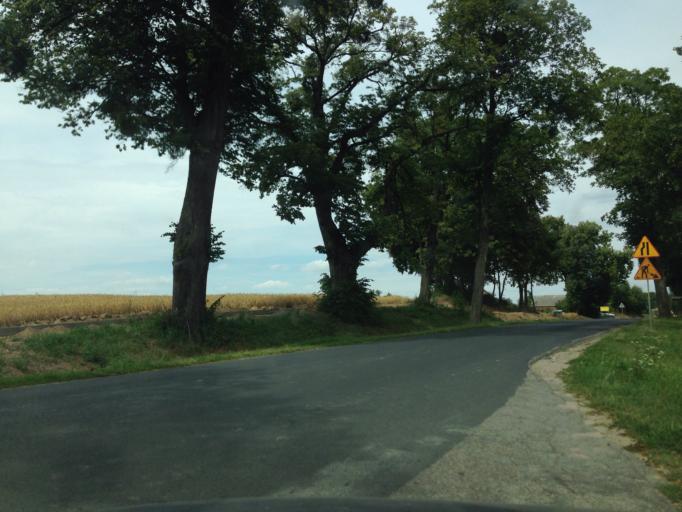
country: PL
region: Kujawsko-Pomorskie
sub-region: Powiat brodnicki
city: Brodnica
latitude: 53.2980
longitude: 19.3978
